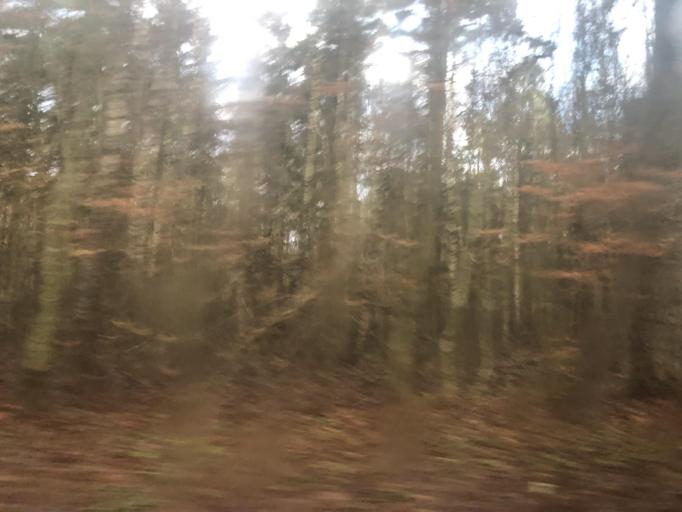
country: SE
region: Skane
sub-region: Sjobo Kommun
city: Blentarp
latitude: 55.6110
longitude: 13.5441
